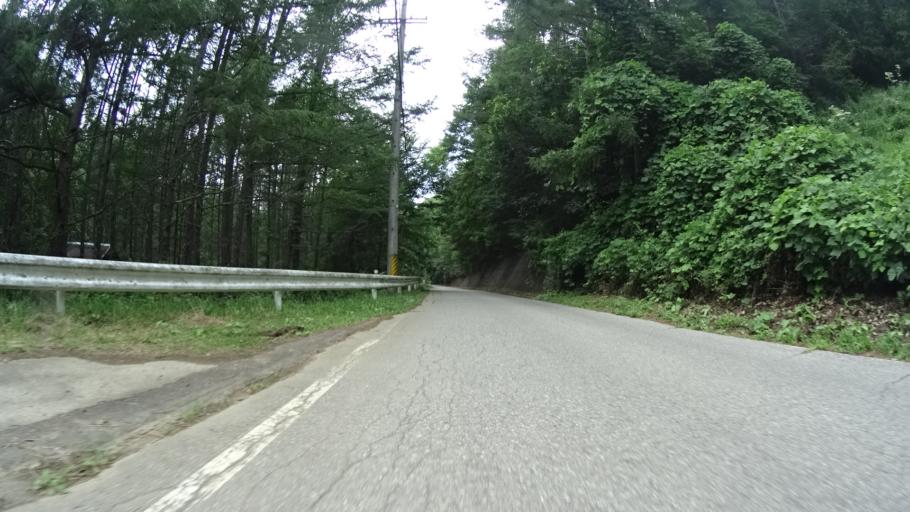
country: JP
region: Nagano
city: Saku
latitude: 36.0702
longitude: 138.6211
